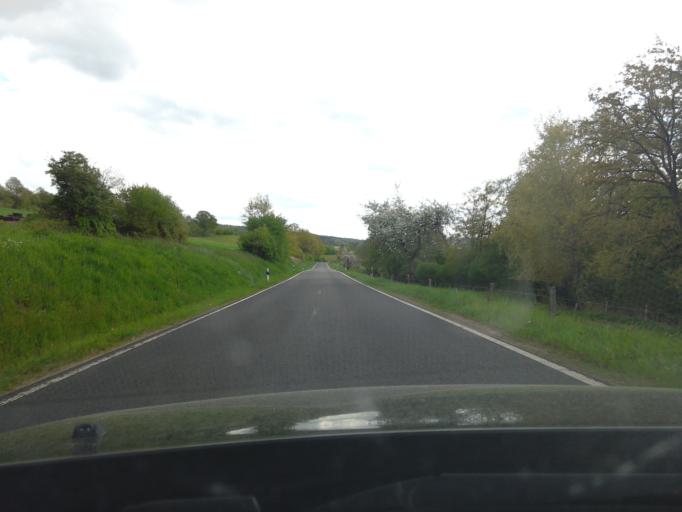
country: DE
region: Hesse
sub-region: Regierungsbezirk Darmstadt
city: Steinau an der Strasse
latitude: 50.2340
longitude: 9.4831
